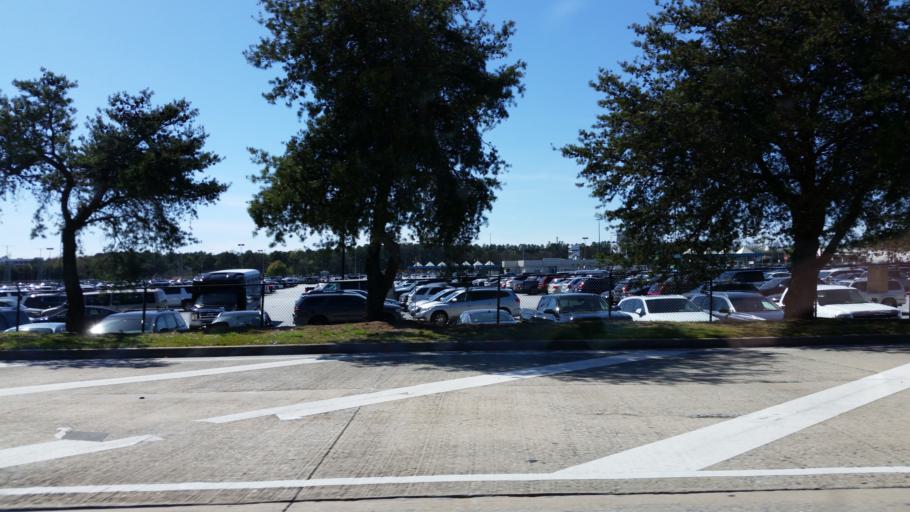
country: US
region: Georgia
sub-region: Fulton County
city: College Park
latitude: 33.6329
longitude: -84.4514
